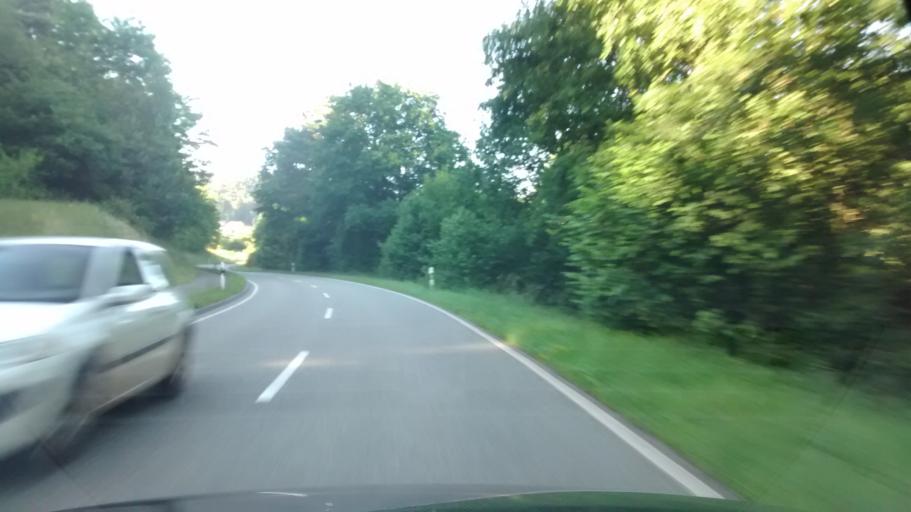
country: DE
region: Rheinland-Pfalz
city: Erfweiler
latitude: 49.1499
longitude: 7.8097
